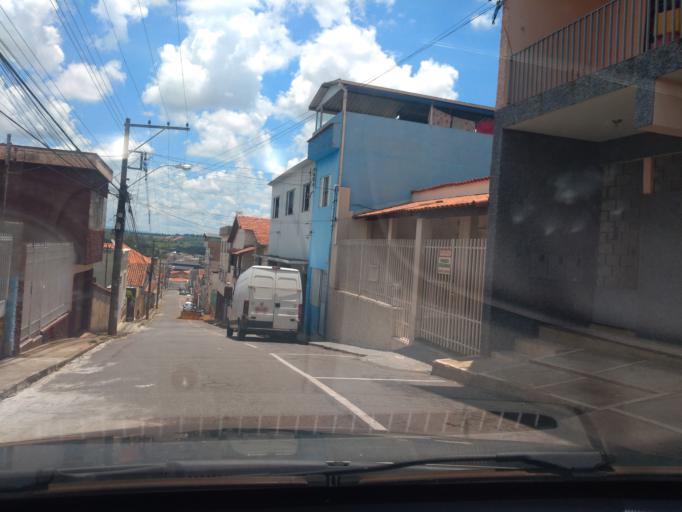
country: BR
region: Minas Gerais
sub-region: Tres Coracoes
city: Tres Coracoes
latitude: -21.6915
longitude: -45.2576
